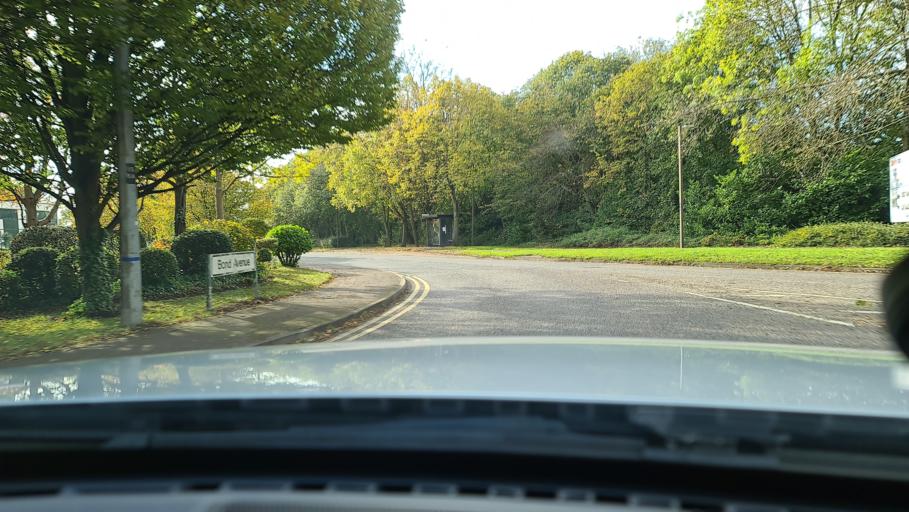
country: GB
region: England
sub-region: Buckinghamshire
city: Bletchley
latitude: 52.0105
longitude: -0.7214
